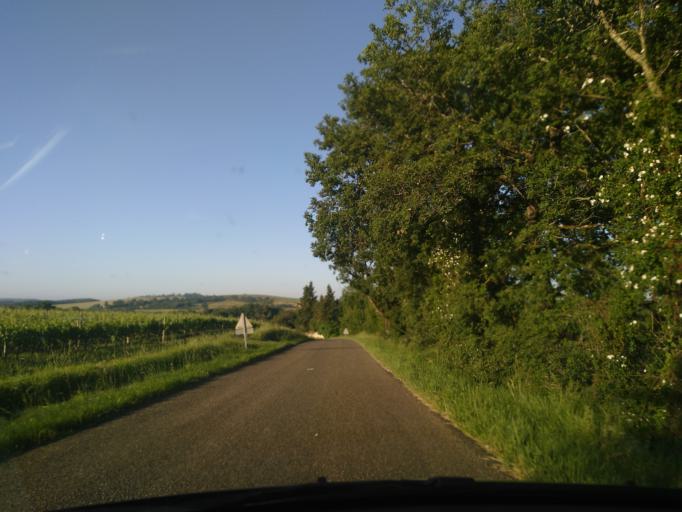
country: FR
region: Midi-Pyrenees
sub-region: Departement du Gers
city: Valence-sur-Baise
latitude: 43.8791
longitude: 0.3976
